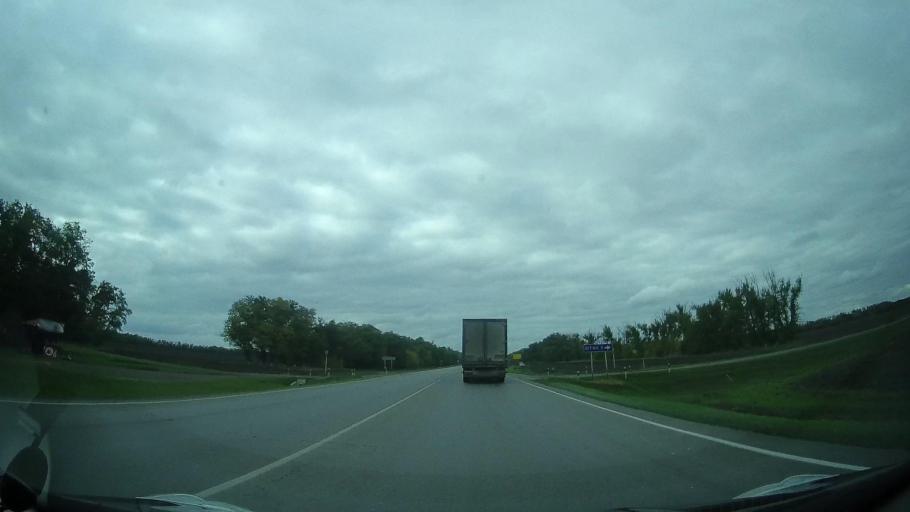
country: RU
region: Rostov
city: Yegorlykskaya
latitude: 46.6237
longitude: 40.5944
